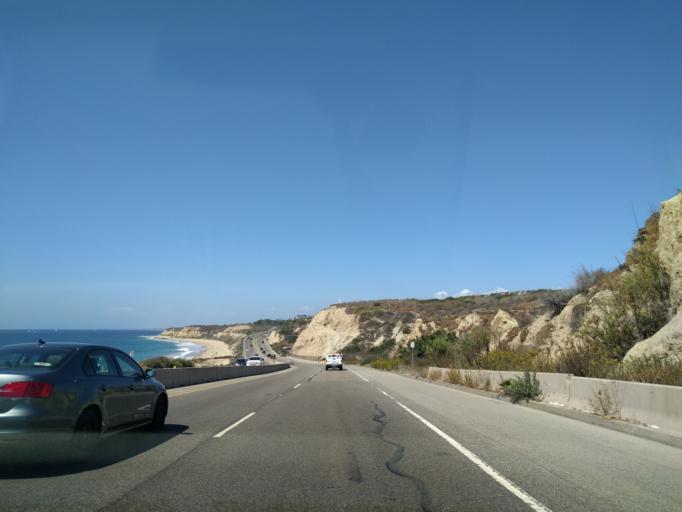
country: US
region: California
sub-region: Orange County
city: Laguna Beach
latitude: 33.5587
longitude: -117.8191
